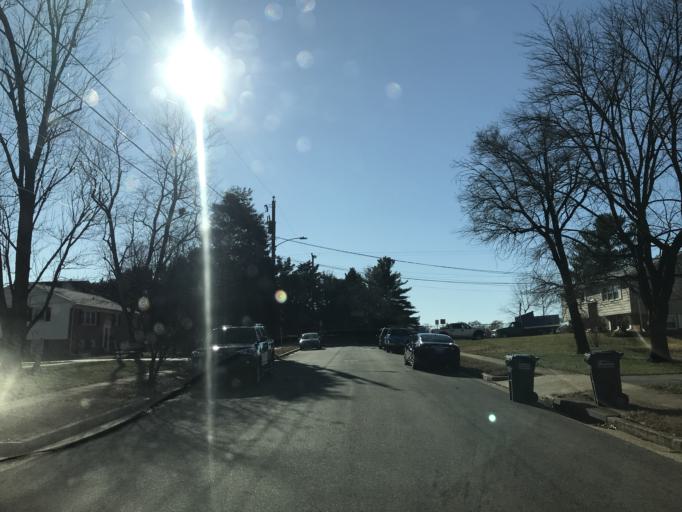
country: US
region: Virginia
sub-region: Fairfax County
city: Franconia
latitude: 38.7836
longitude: -77.1612
